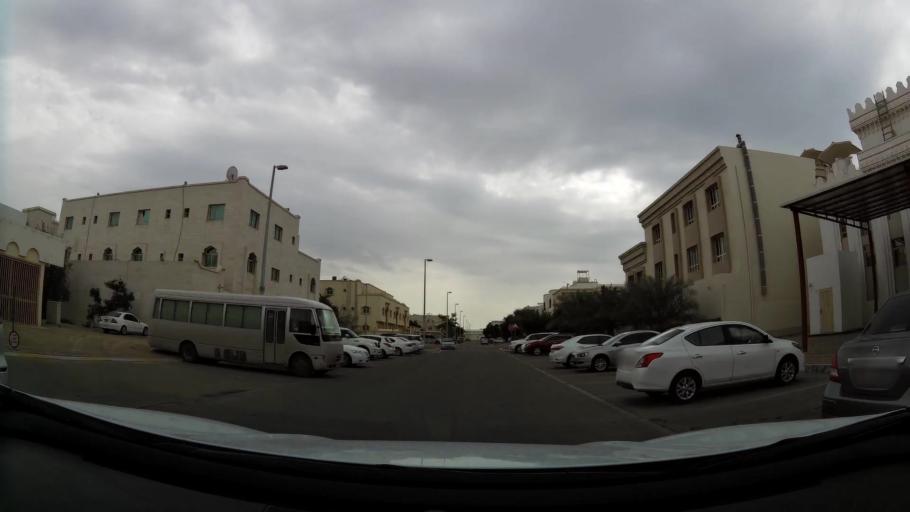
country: AE
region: Abu Dhabi
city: Abu Dhabi
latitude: 24.4264
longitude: 54.4256
